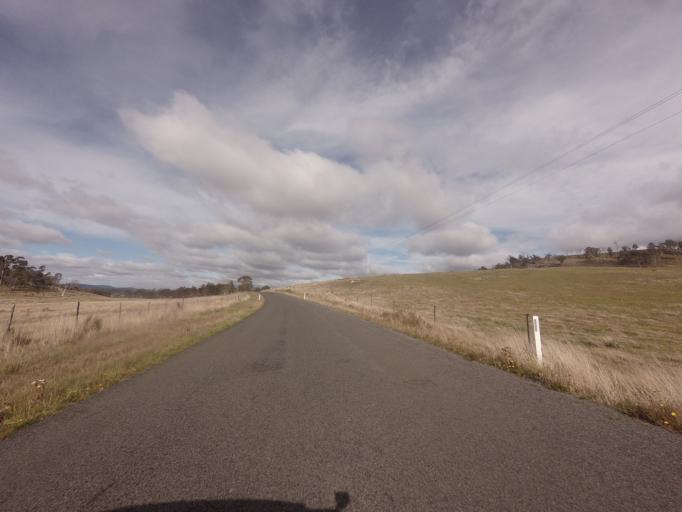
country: AU
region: Tasmania
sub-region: Brighton
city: Bridgewater
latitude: -42.3937
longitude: 147.3665
